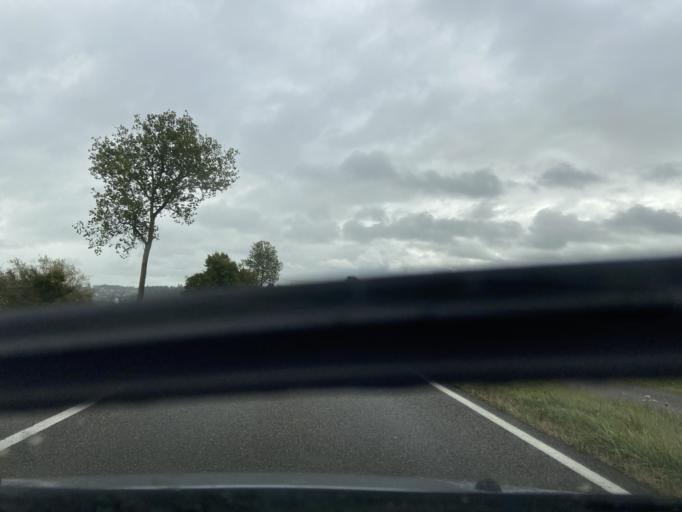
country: DE
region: Baden-Wuerttemberg
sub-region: Tuebingen Region
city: Messkirch
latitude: 48.0021
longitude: 9.1698
